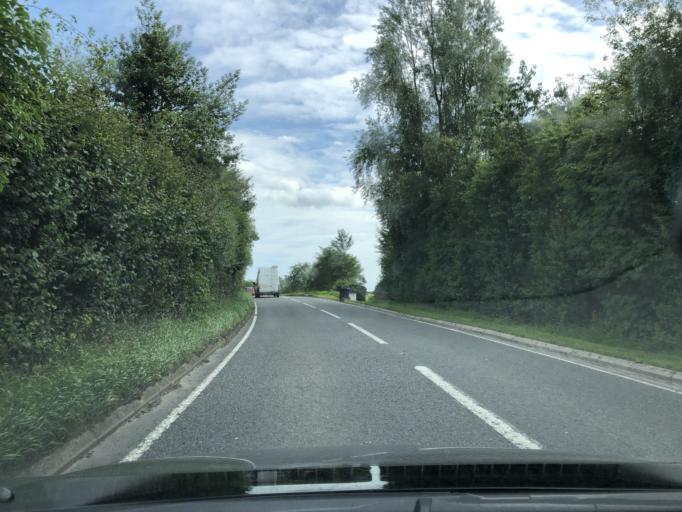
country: GB
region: Northern Ireland
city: Ballynahinch
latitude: 54.4268
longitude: -5.9246
